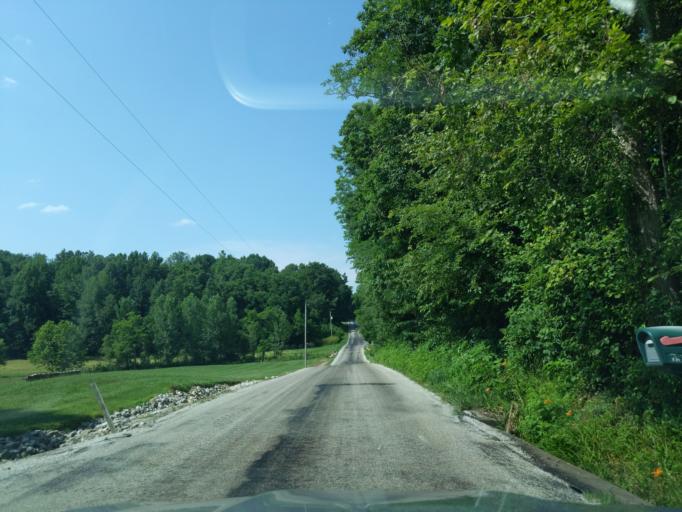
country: US
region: Indiana
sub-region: Ripley County
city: Osgood
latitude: 39.1244
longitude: -85.3418
